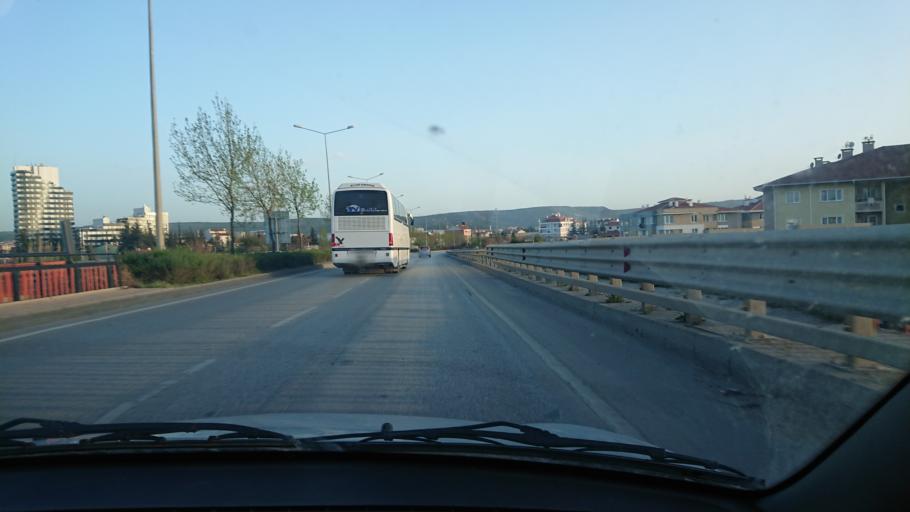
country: TR
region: Eskisehir
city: Eskisehir
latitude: 39.7747
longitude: 30.4837
